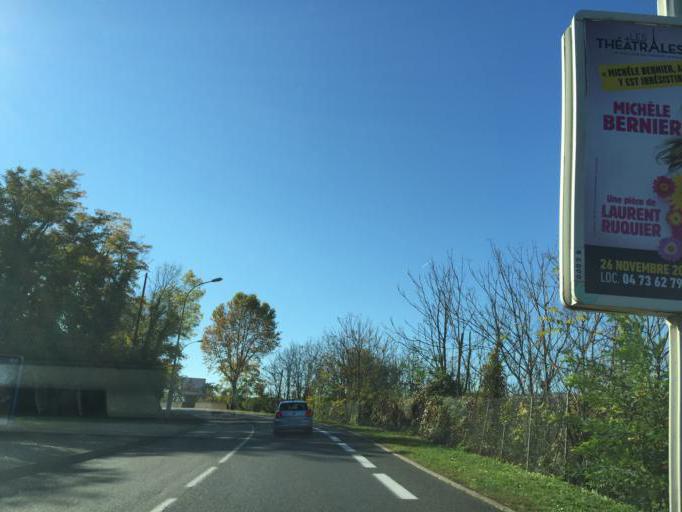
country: FR
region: Rhone-Alpes
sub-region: Departement de la Loire
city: Rive-de-Gier
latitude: 45.5214
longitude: 4.5979
